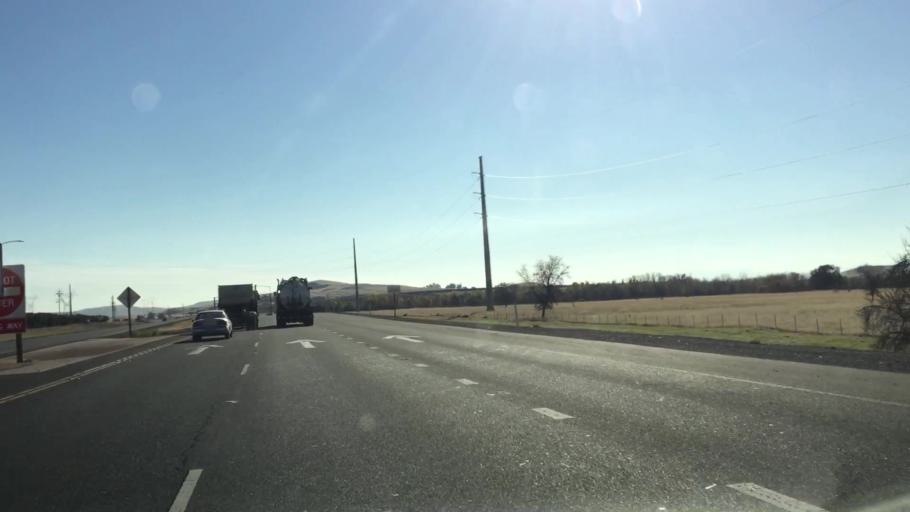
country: US
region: California
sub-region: Butte County
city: Thermalito
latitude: 39.5925
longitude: -121.6204
